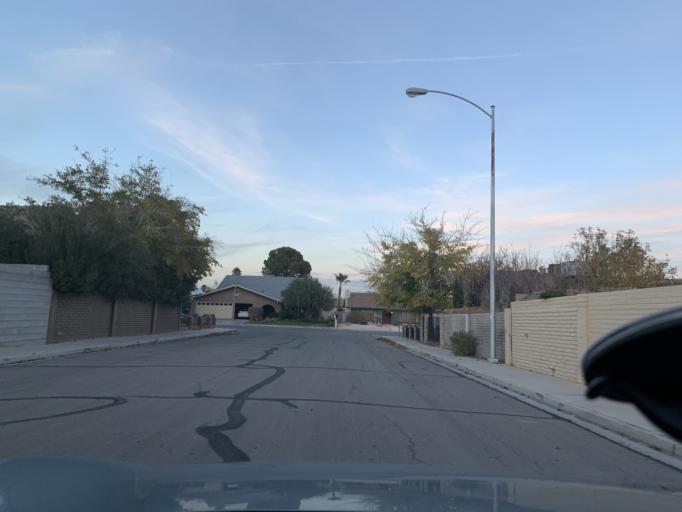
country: US
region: Nevada
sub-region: Clark County
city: Spring Valley
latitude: 36.0938
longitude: -115.2286
